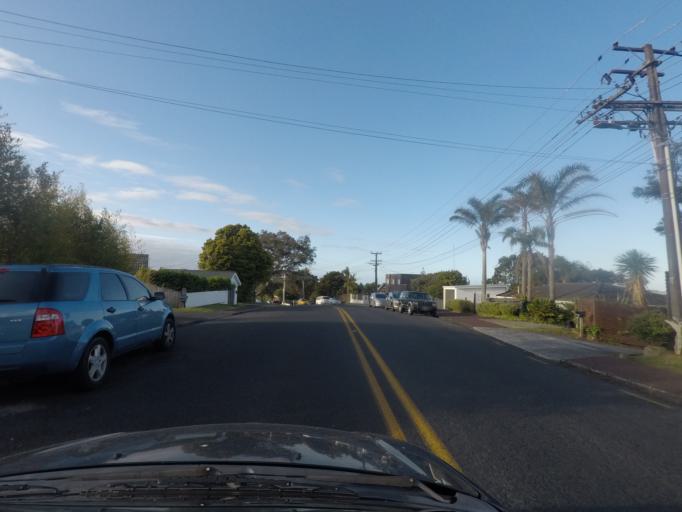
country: NZ
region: Auckland
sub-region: Auckland
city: Waitakere
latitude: -36.9195
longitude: 174.6578
